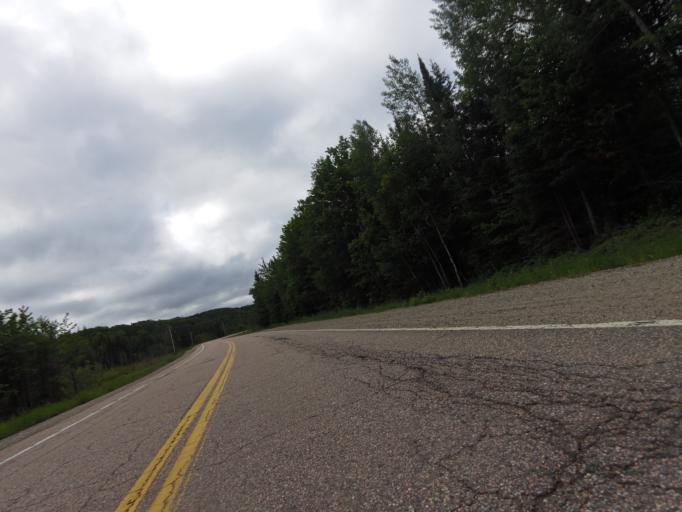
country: CA
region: Quebec
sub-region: Outaouais
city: Shawville
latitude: 45.8154
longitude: -76.4604
